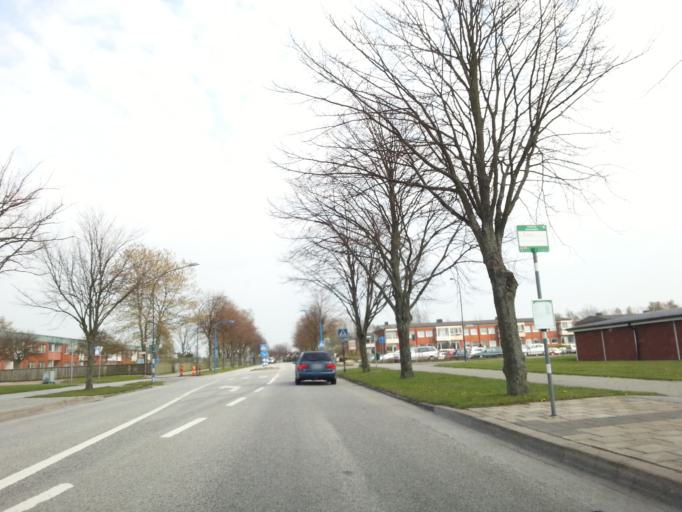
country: SE
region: Skane
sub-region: Trelleborgs Kommun
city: Trelleborg
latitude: 55.3740
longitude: 13.1844
